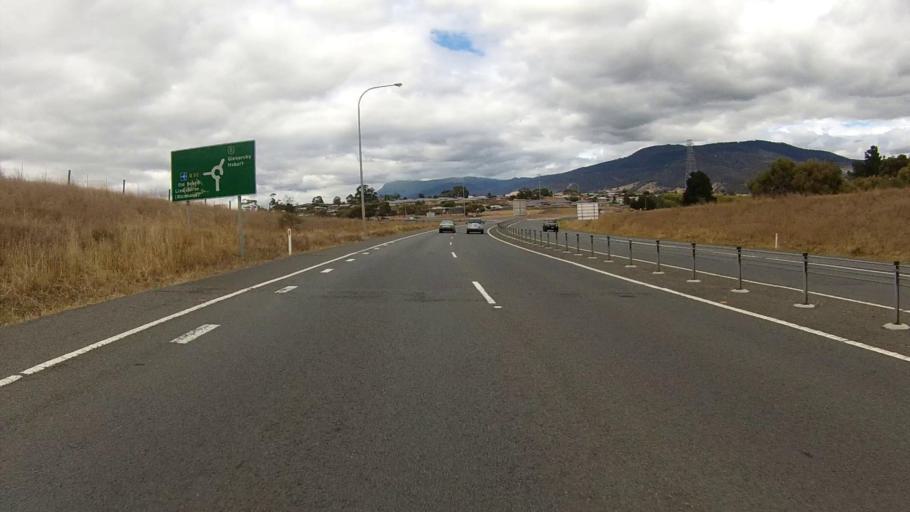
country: AU
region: Tasmania
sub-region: Brighton
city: Bridgewater
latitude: -42.7306
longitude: 147.2379
